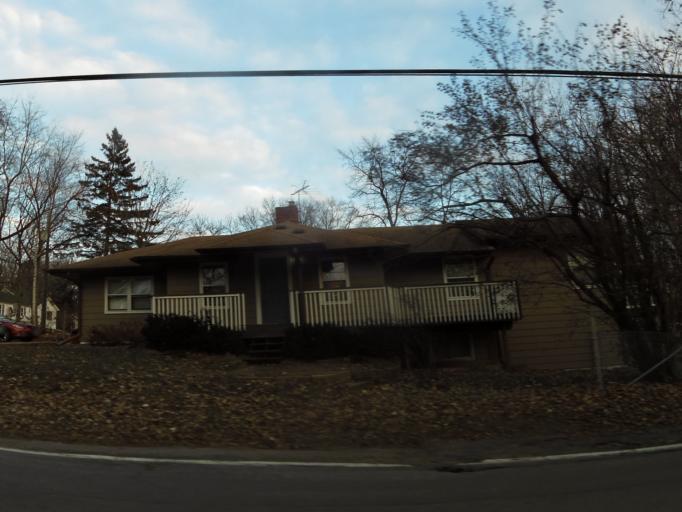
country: US
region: Minnesota
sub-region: Washington County
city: Mahtomedi
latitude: 45.0605
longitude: -92.9584
